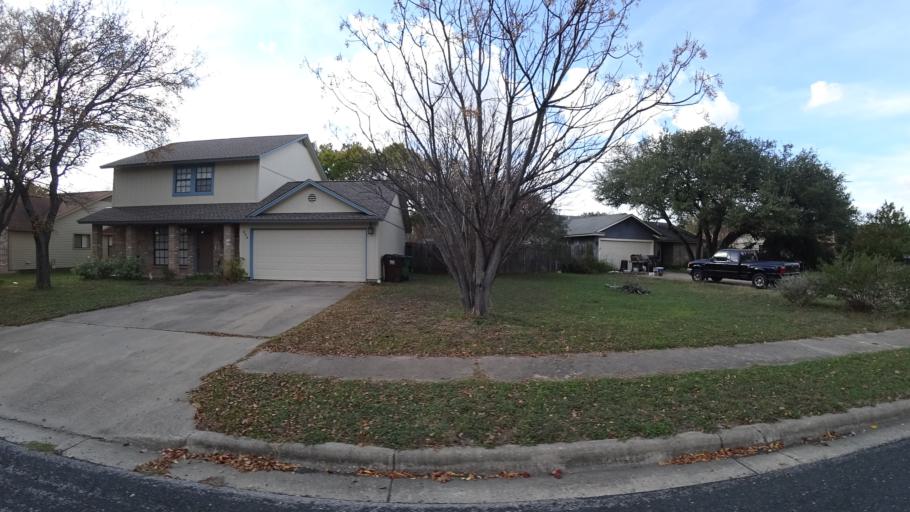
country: US
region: Texas
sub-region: Williamson County
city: Brushy Creek
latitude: 30.5098
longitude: -97.7283
